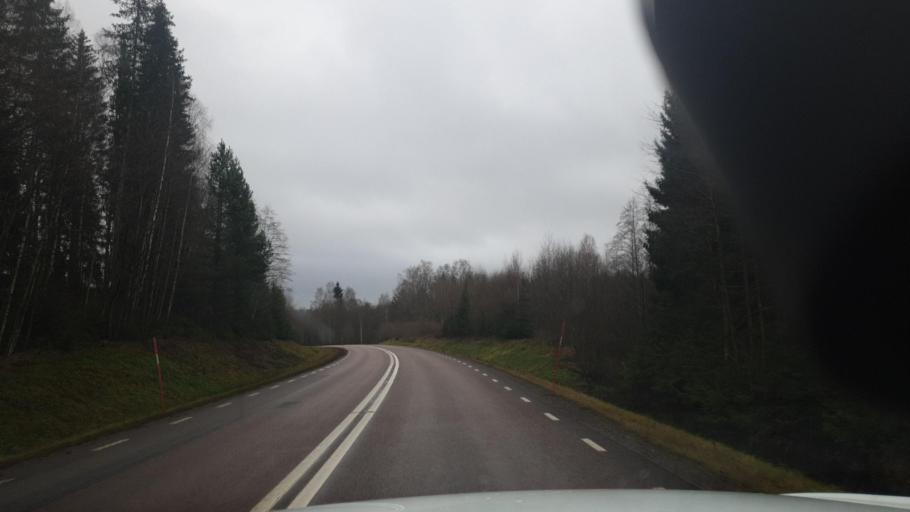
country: SE
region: Vaermland
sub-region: Eda Kommun
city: Amotfors
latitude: 59.6755
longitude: 12.4504
